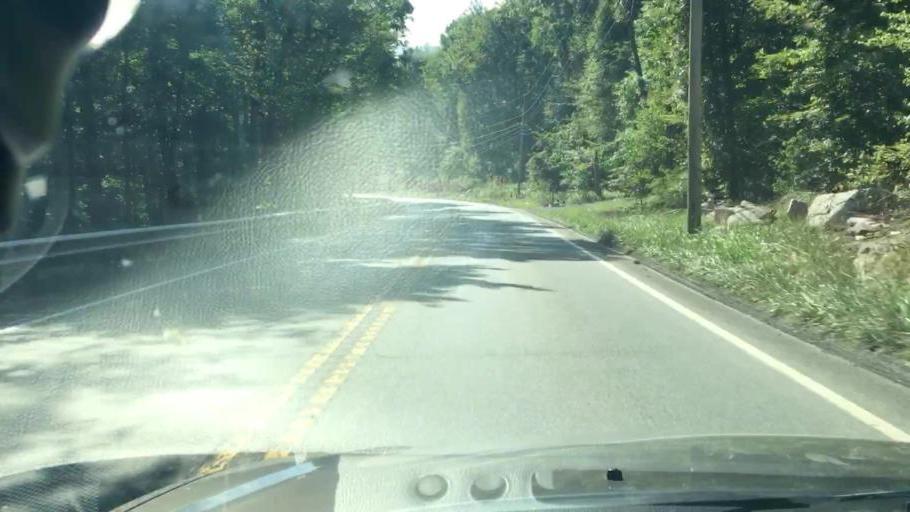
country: US
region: Pennsylvania
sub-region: Carbon County
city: Jim Thorpe
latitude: 40.8867
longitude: -75.7211
